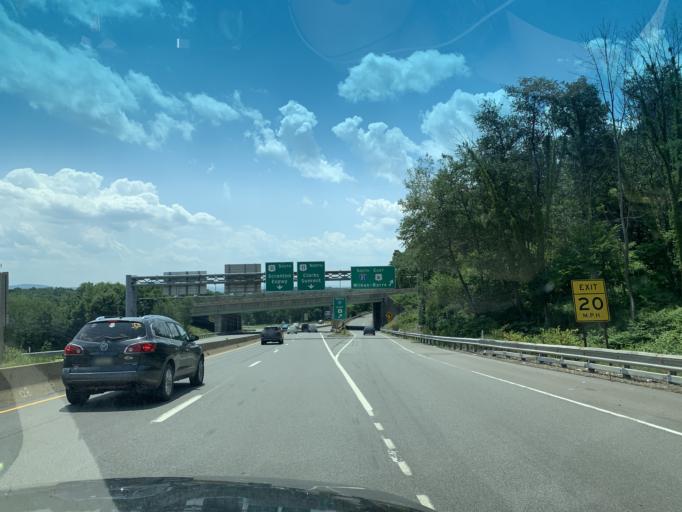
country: US
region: Pennsylvania
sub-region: Lackawanna County
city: Chinchilla
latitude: 41.4580
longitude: -75.6594
